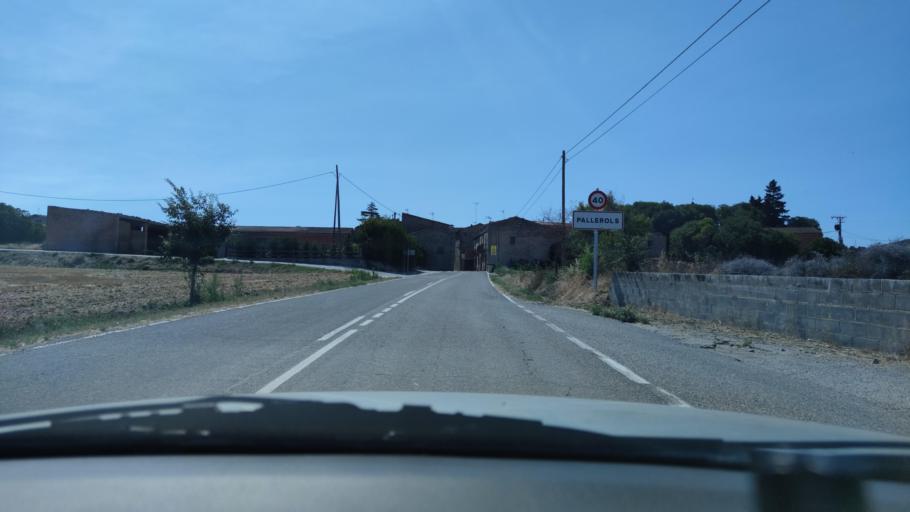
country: ES
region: Catalonia
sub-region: Provincia de Lleida
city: Sant Guim de Freixenet
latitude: 41.6199
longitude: 1.3521
